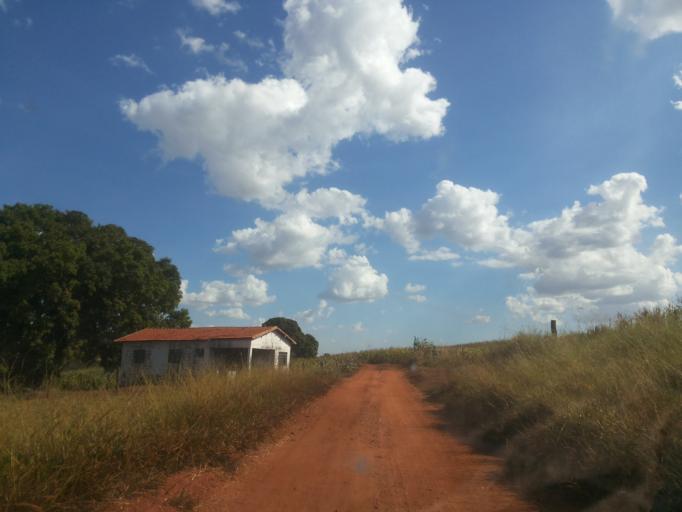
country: BR
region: Minas Gerais
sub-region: Capinopolis
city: Capinopolis
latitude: -18.5807
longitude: -49.4925
